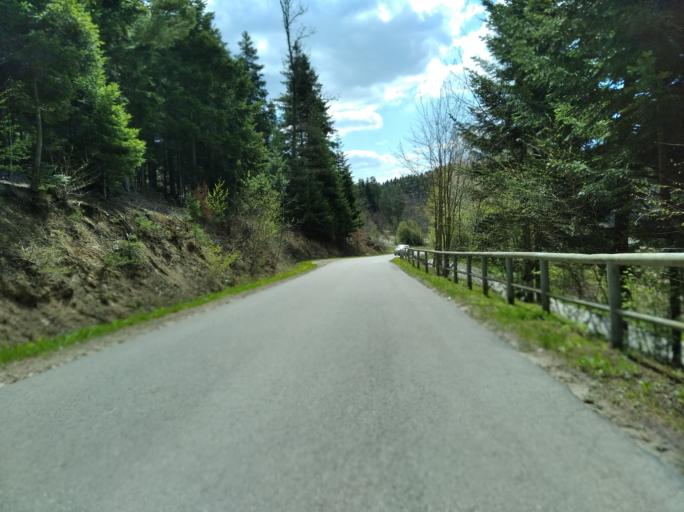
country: PL
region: Subcarpathian Voivodeship
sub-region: Powiat brzozowski
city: Wesola
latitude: 49.7566
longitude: 22.1225
